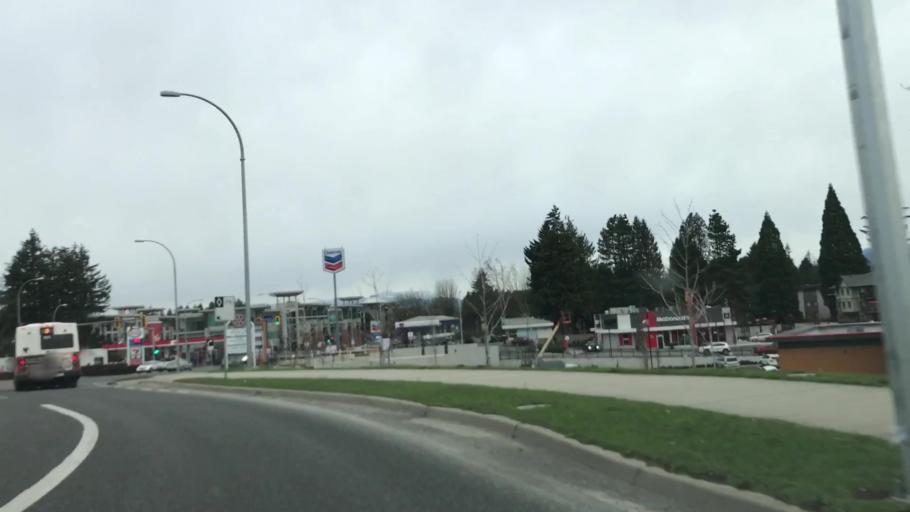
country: US
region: Washington
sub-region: Whatcom County
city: Sumas
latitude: 49.0352
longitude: -122.2925
